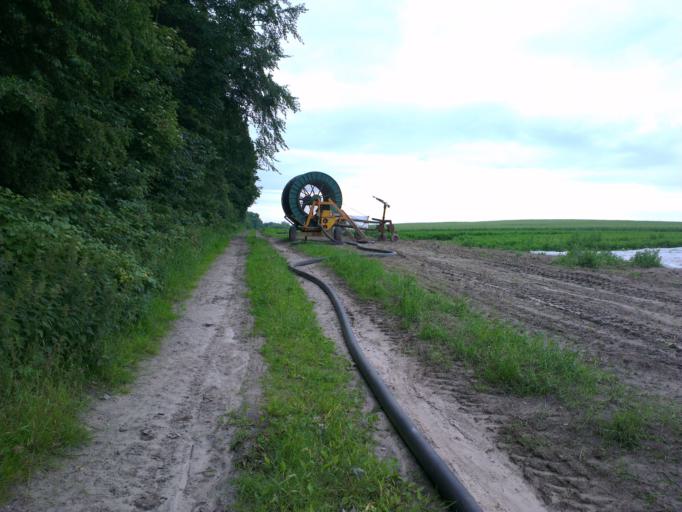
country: DK
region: Capital Region
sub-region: Frederikssund Kommune
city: Skibby
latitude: 55.7857
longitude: 11.9527
